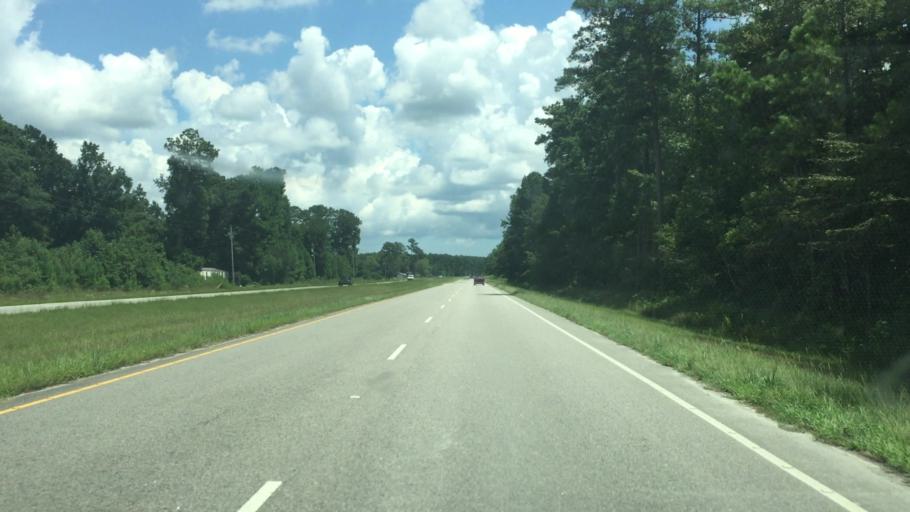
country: US
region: South Carolina
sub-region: Horry County
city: Loris
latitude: 34.0104
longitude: -78.7728
